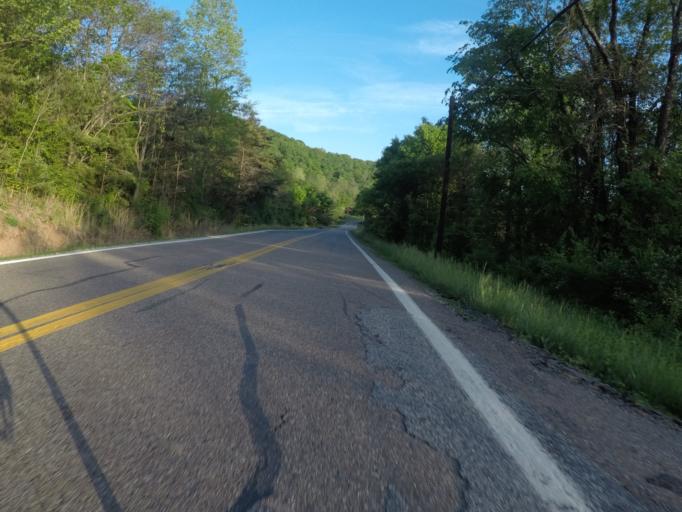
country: US
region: West Virginia
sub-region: Cabell County
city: Huntington
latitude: 38.5030
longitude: -82.4768
